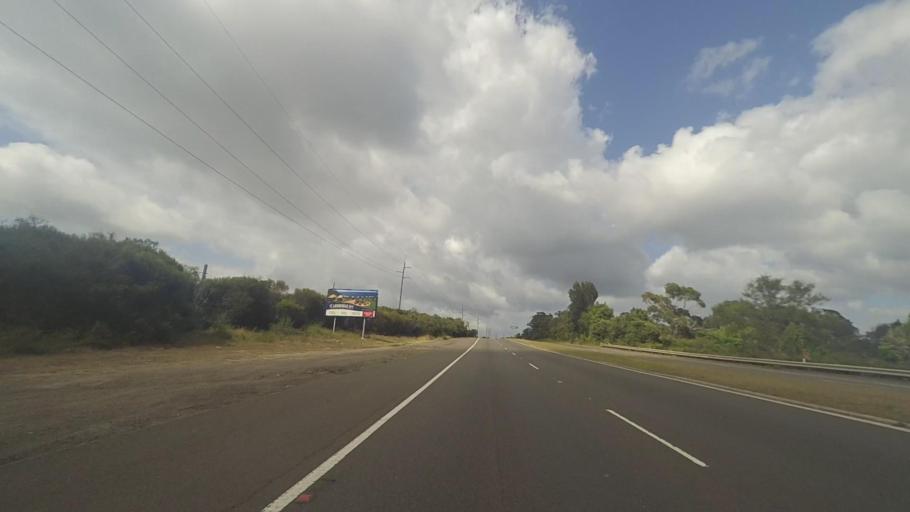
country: AU
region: New South Wales
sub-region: Sutherland Shire
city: Heathcote
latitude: -34.0948
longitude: 151.0003
